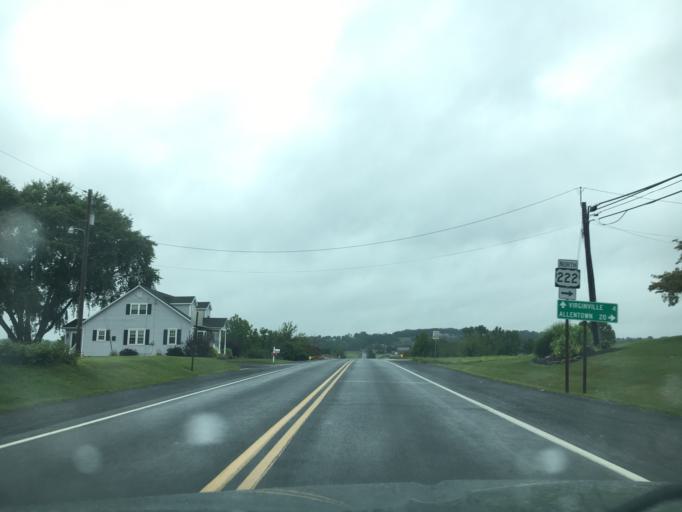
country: US
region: Pennsylvania
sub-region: Berks County
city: Kutztown
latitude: 40.5033
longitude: -75.8042
